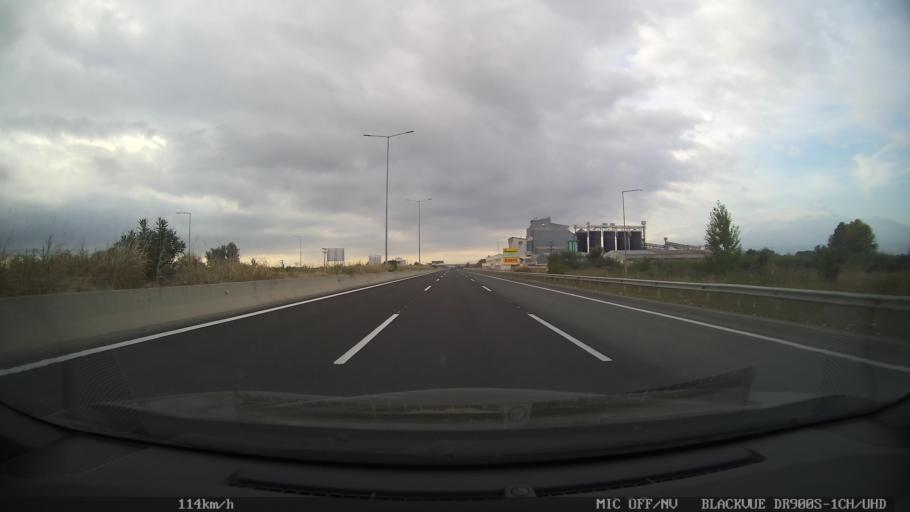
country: GR
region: Central Macedonia
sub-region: Nomos Pierias
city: Peristasi
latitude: 40.2500
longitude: 22.5332
